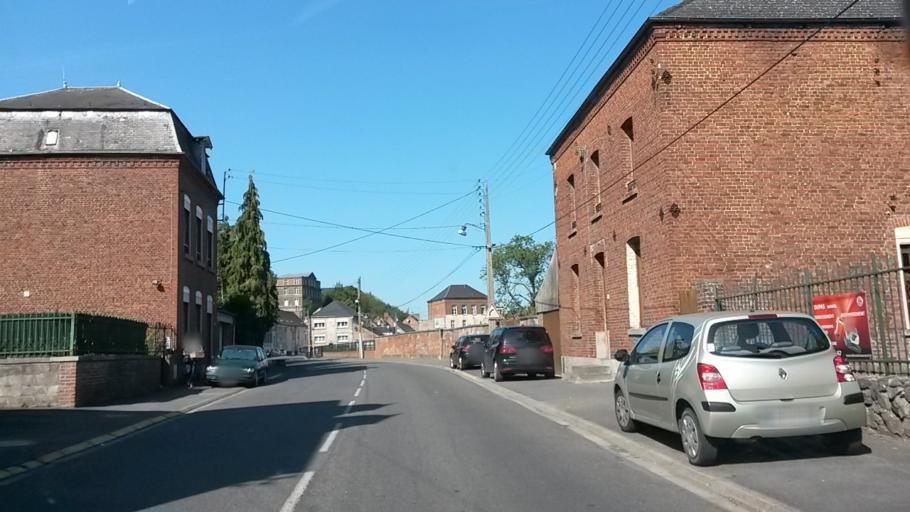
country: FR
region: Nord-Pas-de-Calais
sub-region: Departement du Nord
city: Avesnes-sur-Helpe
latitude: 50.1229
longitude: 3.9357
